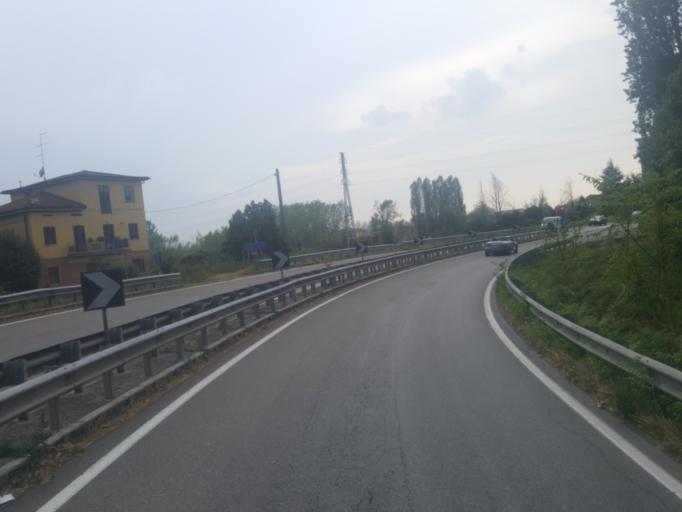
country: IT
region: Emilia-Romagna
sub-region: Provincia di Modena
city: San Damaso
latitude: 44.6196
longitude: 10.9912
